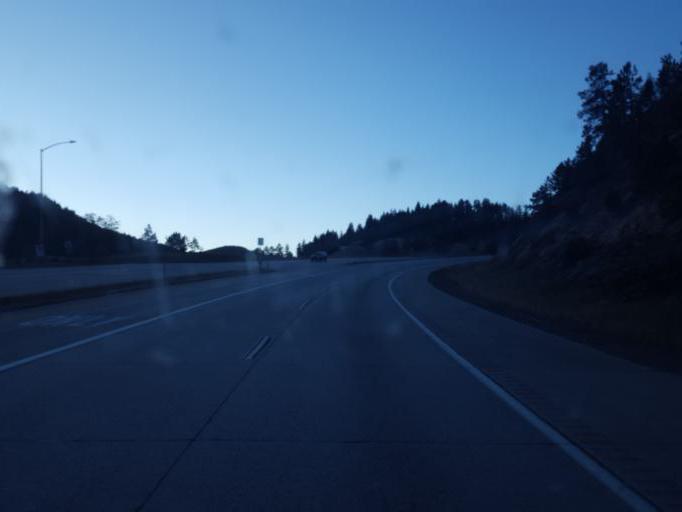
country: US
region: Colorado
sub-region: Jefferson County
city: Indian Hills
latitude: 39.6074
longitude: -105.2308
